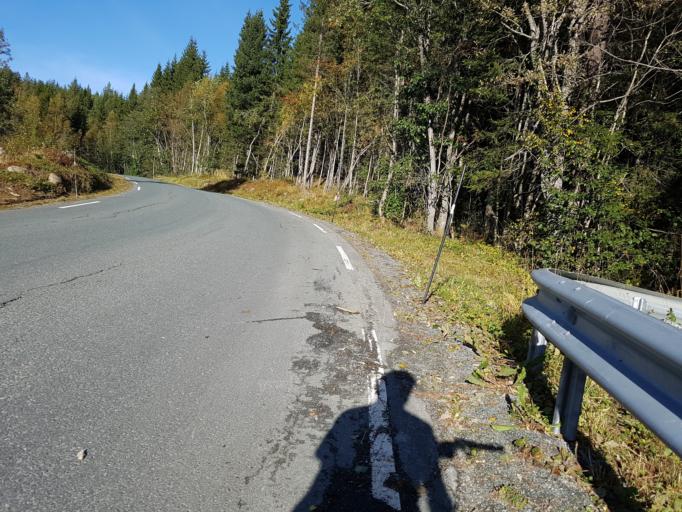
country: NO
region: Sor-Trondelag
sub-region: Klaebu
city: Klaebu
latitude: 63.3467
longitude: 10.5376
